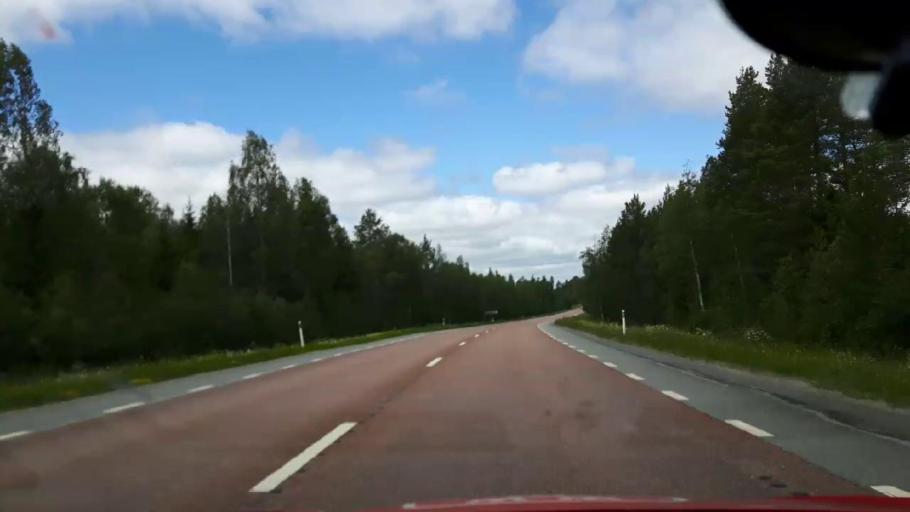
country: SE
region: Jaemtland
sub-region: Braecke Kommun
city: Braecke
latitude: 62.8185
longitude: 15.3365
